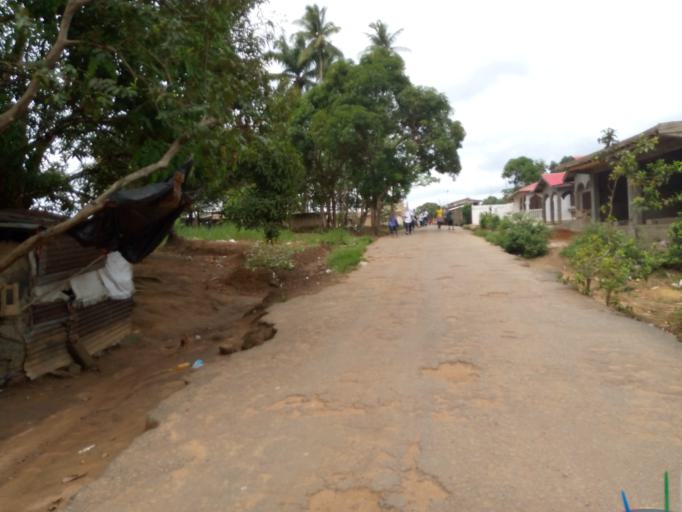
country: SL
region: Western Area
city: Waterloo
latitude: 8.3349
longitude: -13.0057
